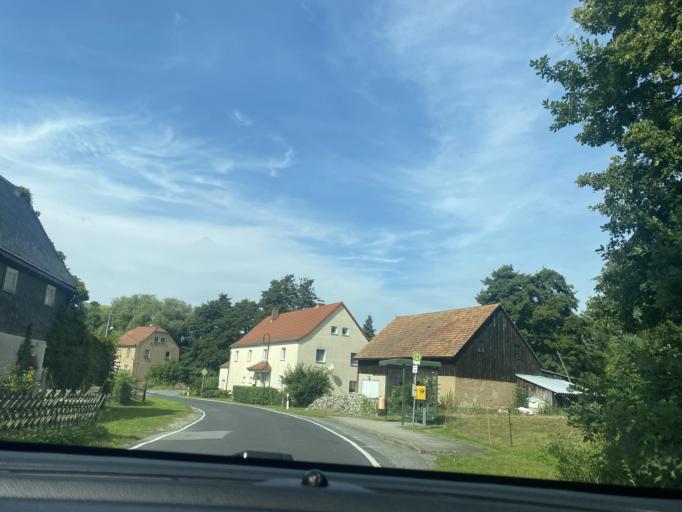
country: DE
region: Saxony
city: Sohland am Rotstein
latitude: 51.1023
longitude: 14.7911
